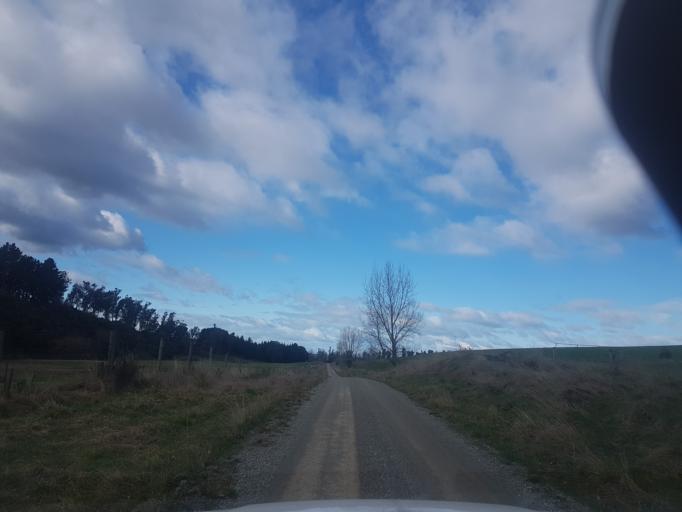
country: NZ
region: Canterbury
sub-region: Timaru District
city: Pleasant Point
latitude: -44.1853
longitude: 171.1468
